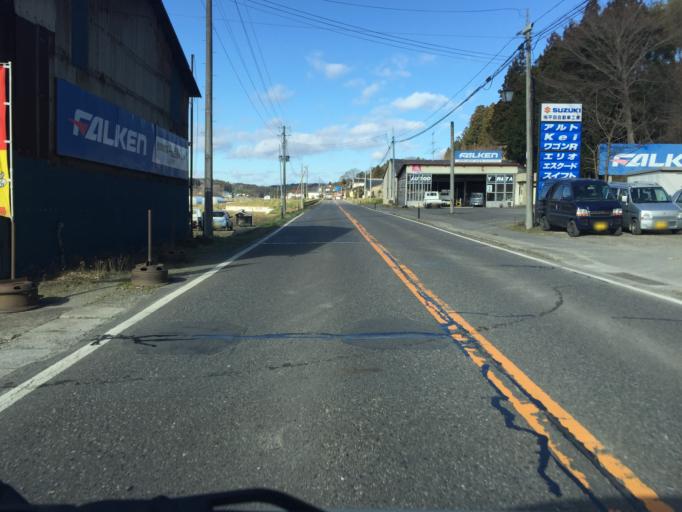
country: JP
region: Fukushima
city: Ishikawa
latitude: 37.2525
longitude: 140.5601
